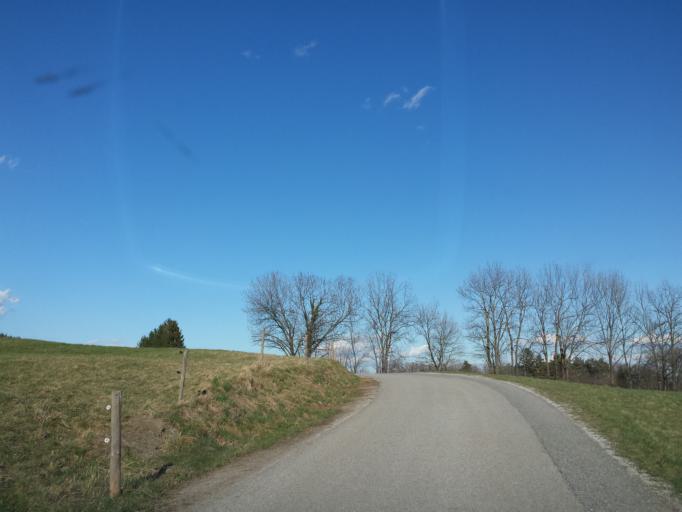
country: AT
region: Styria
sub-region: Politischer Bezirk Graz-Umgebung
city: Sankt Radegund bei Graz
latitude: 47.1538
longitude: 15.4551
